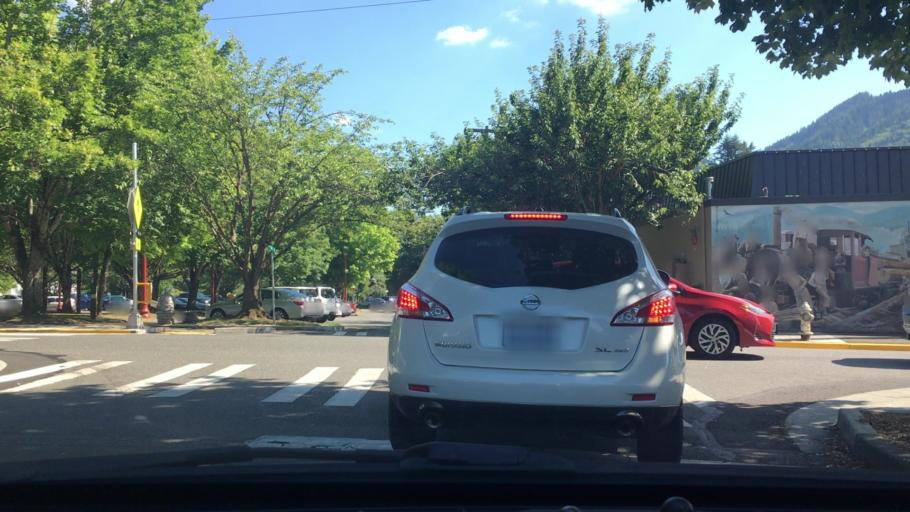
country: US
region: Washington
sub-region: King County
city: Issaquah
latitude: 47.5303
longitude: -122.0352
